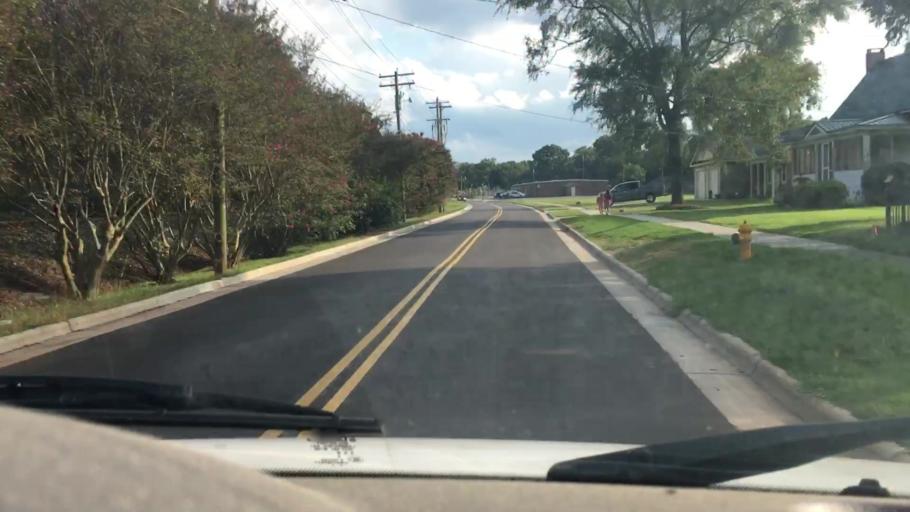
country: US
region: North Carolina
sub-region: Mecklenburg County
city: Huntersville
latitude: 35.4147
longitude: -80.8410
